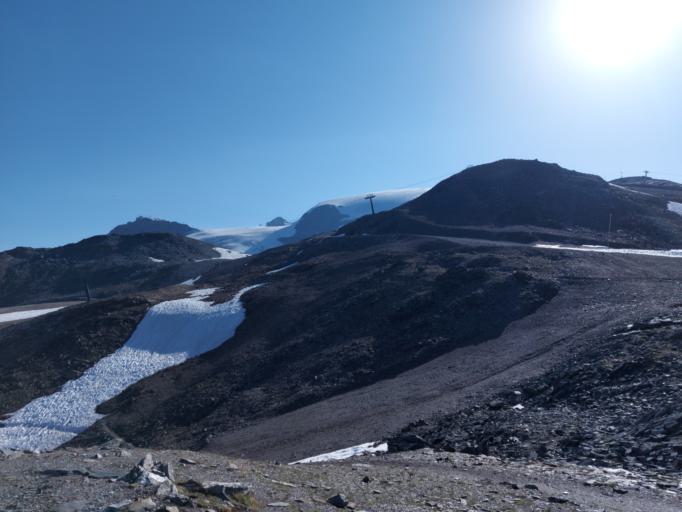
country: IT
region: Aosta Valley
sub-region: Valle d'Aosta
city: Paquier
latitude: 45.9185
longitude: 7.6855
